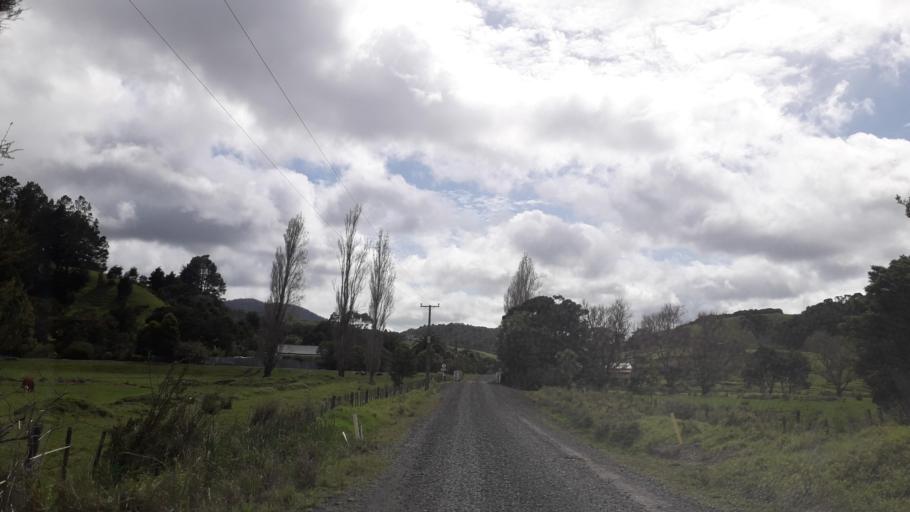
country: NZ
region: Northland
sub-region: Far North District
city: Ahipara
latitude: -35.2466
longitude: 173.2515
